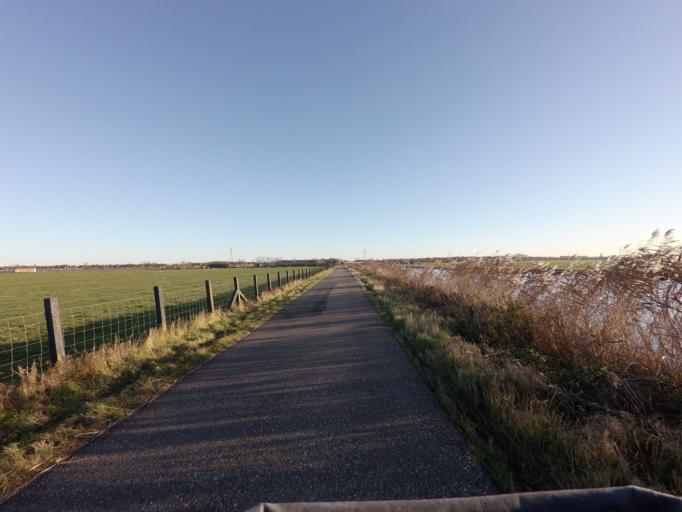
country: NL
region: Utrecht
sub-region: Stichtse Vecht
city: Breukelen
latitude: 52.2055
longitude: 4.9894
